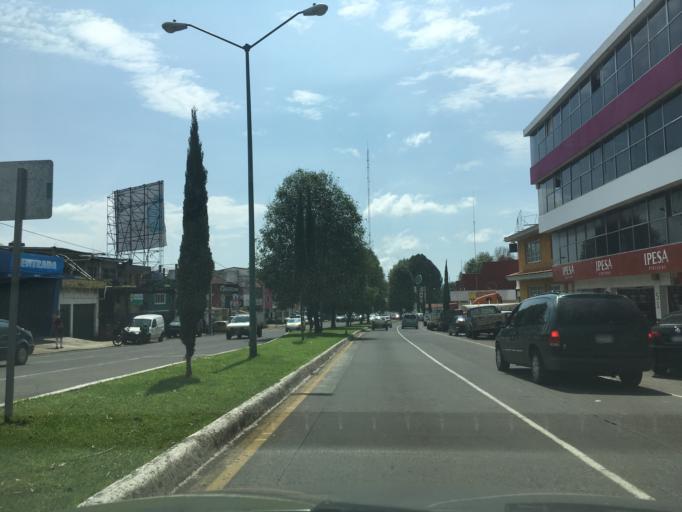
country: MX
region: Michoacan
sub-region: Uruapan
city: Uruapan
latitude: 19.4243
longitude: -102.0480
